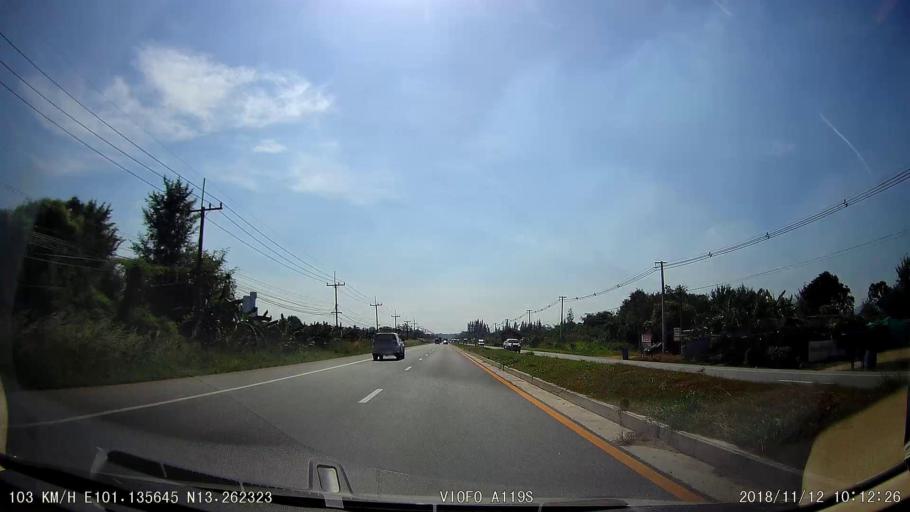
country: TH
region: Chon Buri
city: Ban Bueng
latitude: 13.2620
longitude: 101.1359
